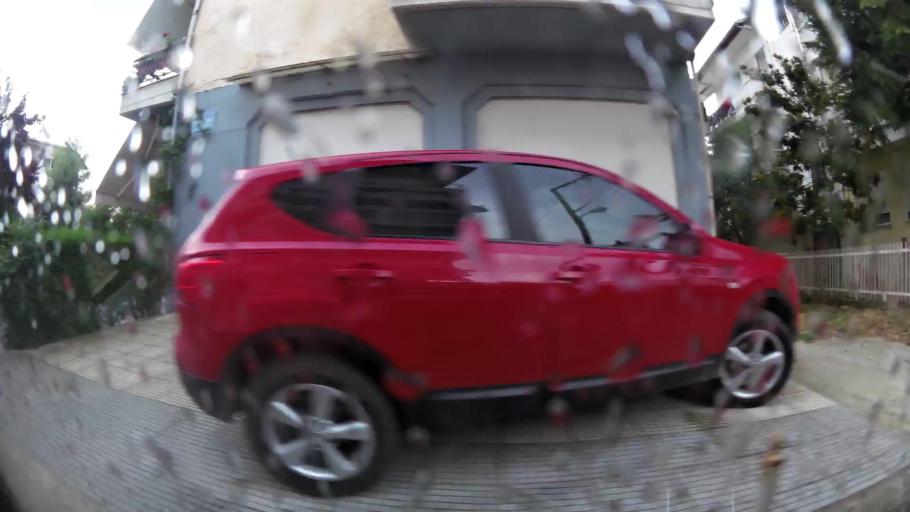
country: GR
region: Central Macedonia
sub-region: Nomos Imathias
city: Veroia
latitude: 40.5269
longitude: 22.1960
